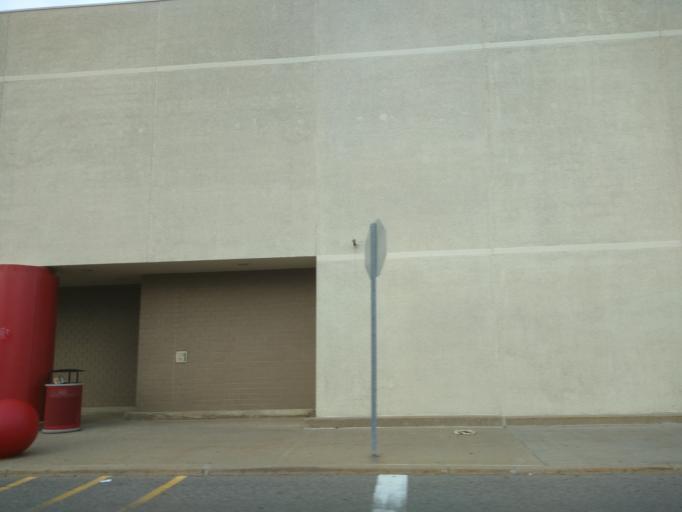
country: US
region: Michigan
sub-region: Ingham County
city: Okemos
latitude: 42.7242
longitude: -84.4133
